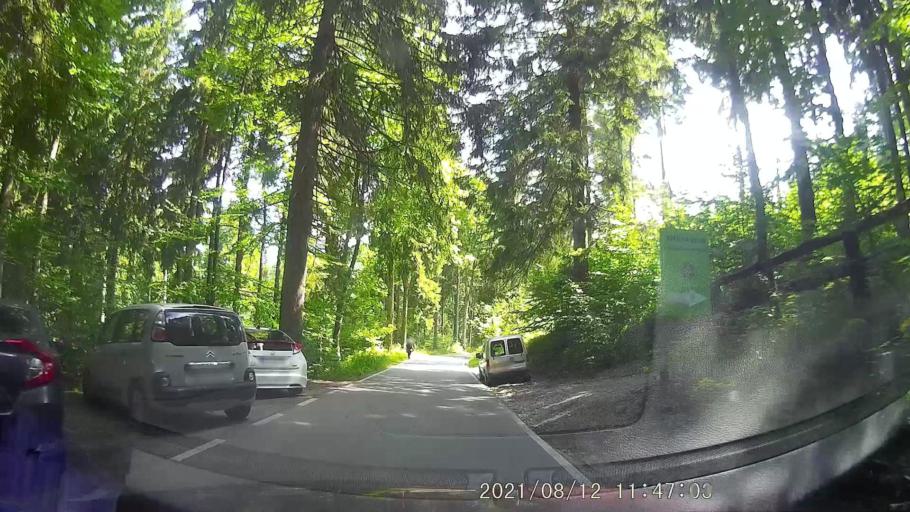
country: PL
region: Lower Silesian Voivodeship
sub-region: Powiat klodzki
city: Stronie Slaskie
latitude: 50.2484
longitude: 16.8450
